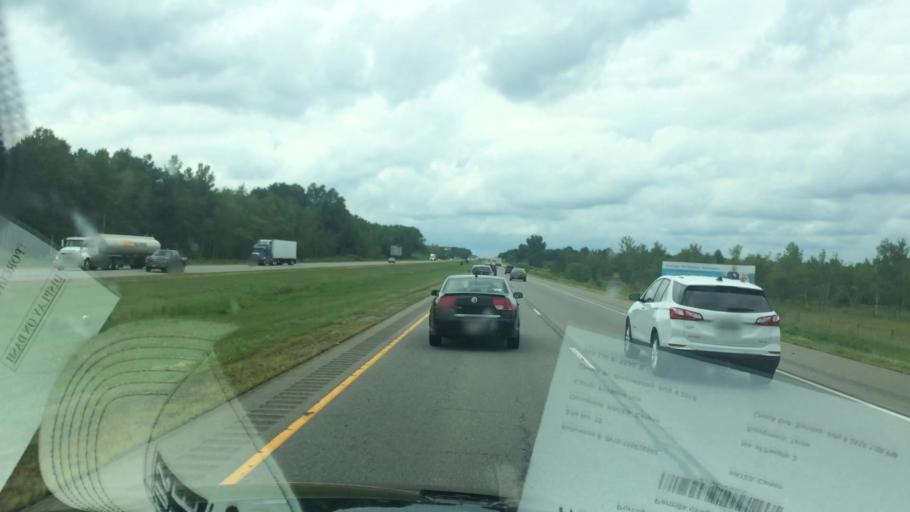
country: US
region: Wisconsin
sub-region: Marathon County
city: Mosinee
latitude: 44.7453
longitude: -89.6797
